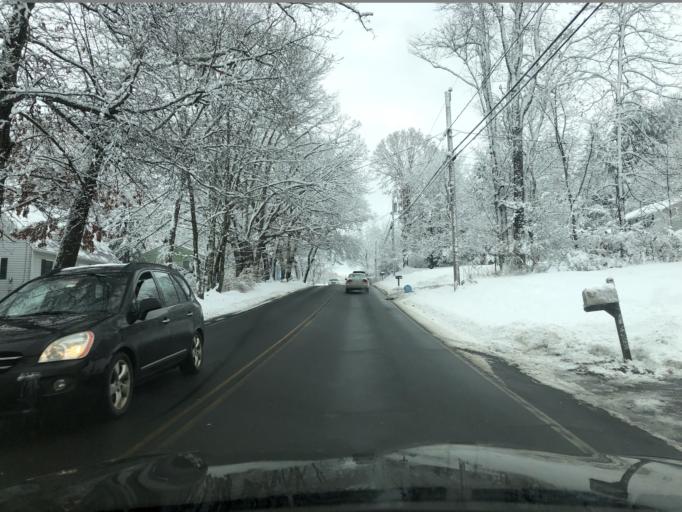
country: US
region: New Hampshire
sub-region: Strafford County
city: Somersworth
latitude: 43.2370
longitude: -70.8630
